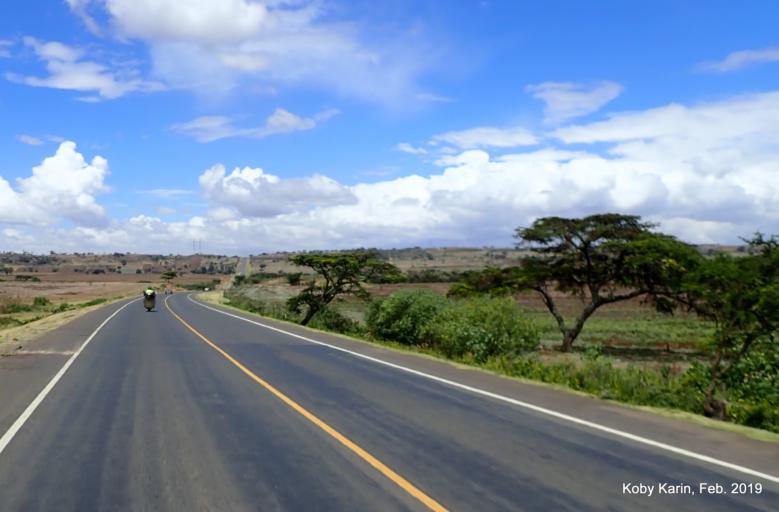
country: KE
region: Narok
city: Narok
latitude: -1.0983
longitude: 36.1445
